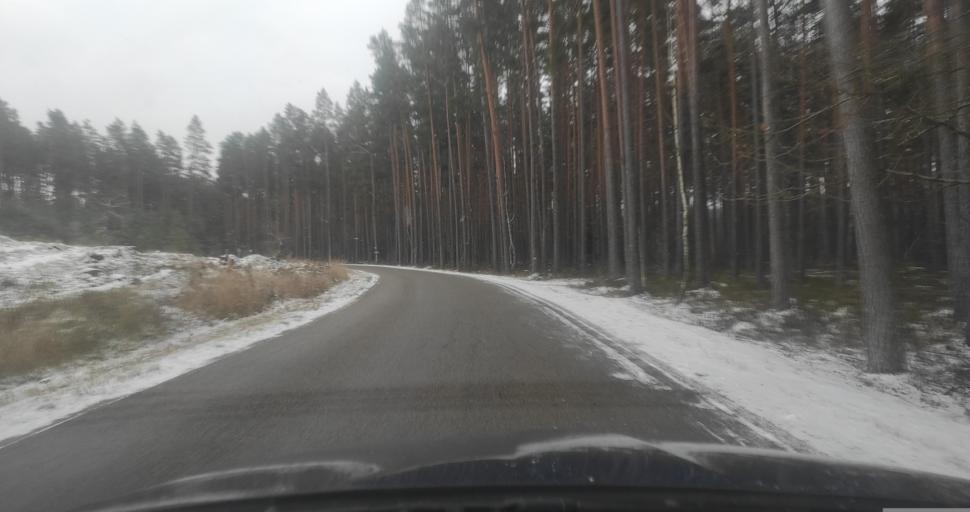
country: LV
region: Jurmala
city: Jurmala
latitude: 56.9112
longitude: 23.8235
